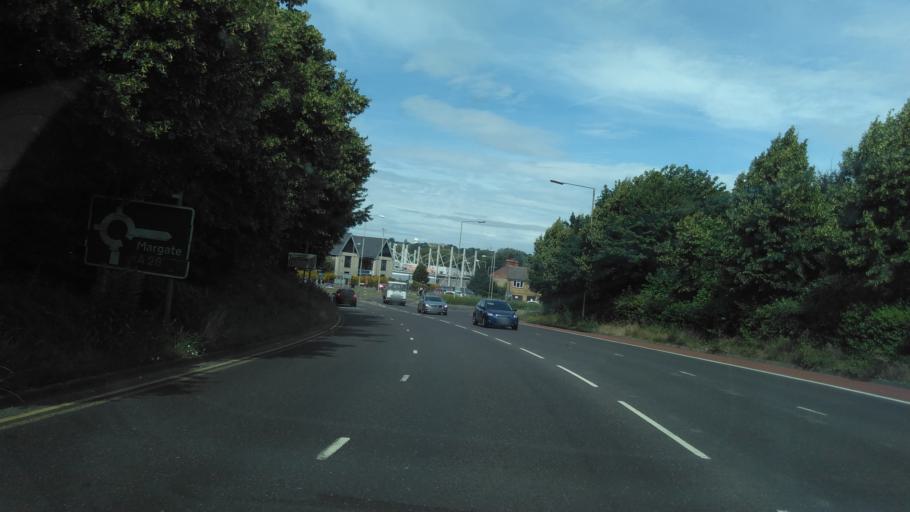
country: GB
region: England
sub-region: Kent
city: Canterbury
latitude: 51.2840
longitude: 1.0891
